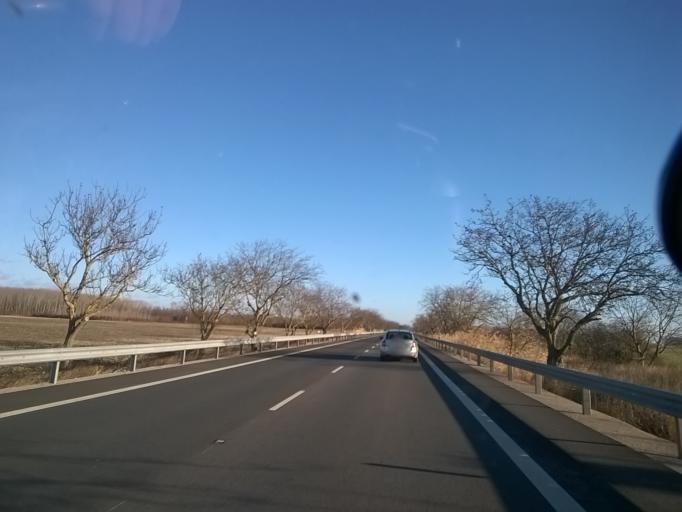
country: SK
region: Trnavsky
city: Sladkovicovo
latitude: 48.1970
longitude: 17.5785
